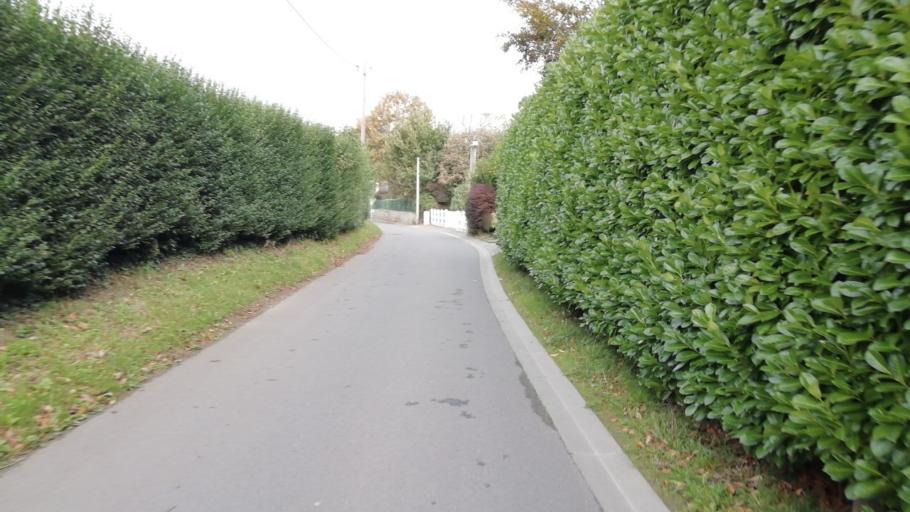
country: FR
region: Haute-Normandie
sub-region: Departement de la Seine-Maritime
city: Octeville-sur-Mer
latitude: 49.5669
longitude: 0.1158
